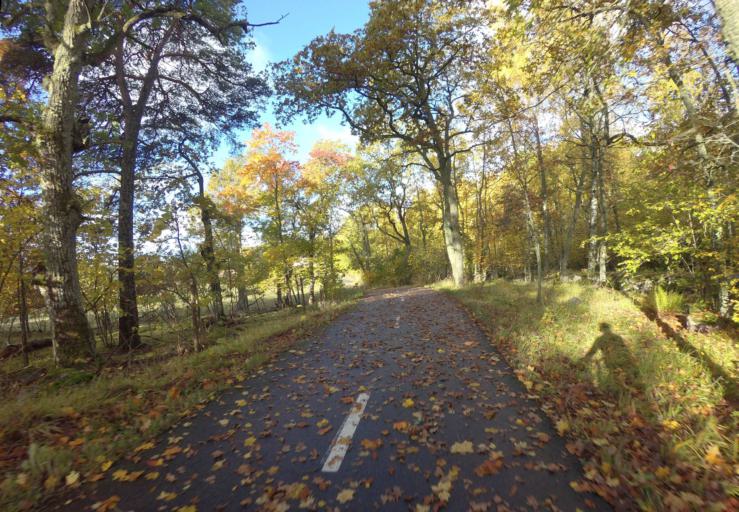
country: FI
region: Varsinais-Suomi
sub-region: Turku
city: Raisio
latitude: 60.4269
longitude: 22.1405
